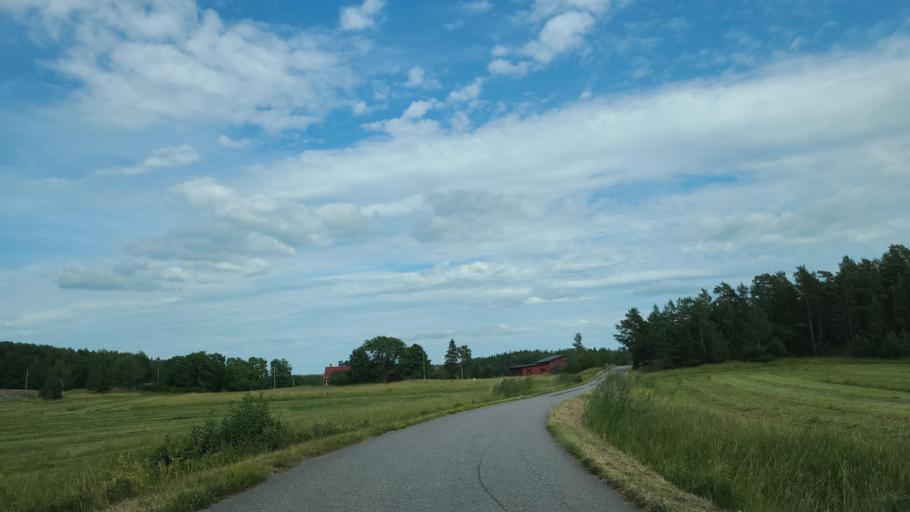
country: FI
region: Varsinais-Suomi
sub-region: Turku
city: Rymaettylae
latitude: 60.2905
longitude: 21.9557
